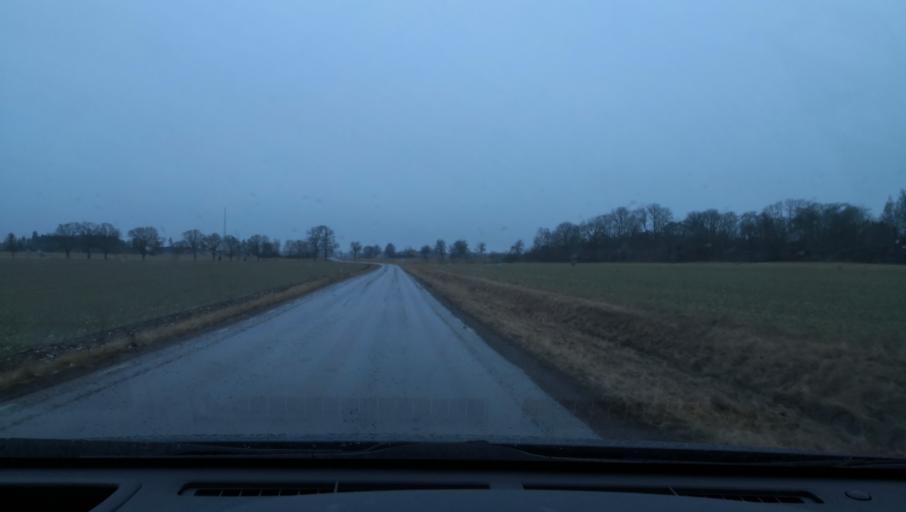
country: SE
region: Soedermanland
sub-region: Eskilstuna Kommun
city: Arla
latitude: 59.4465
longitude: 16.7222
